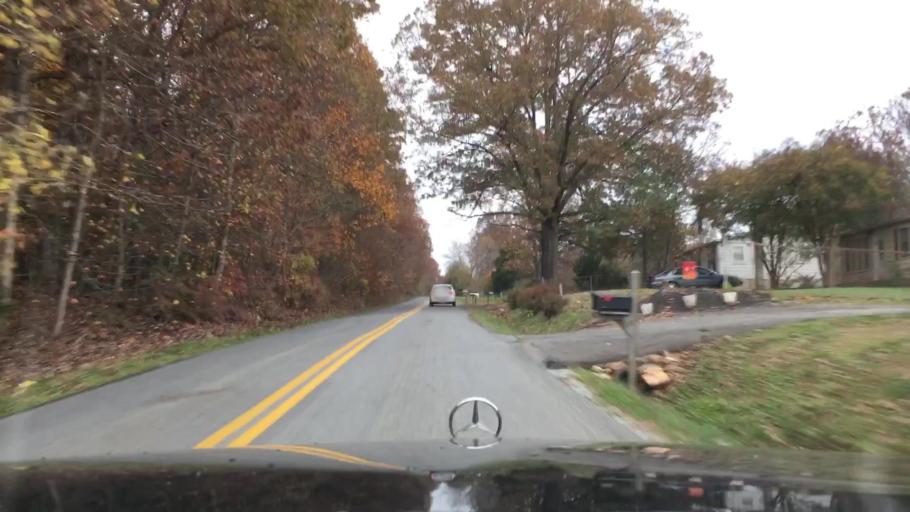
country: US
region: Virginia
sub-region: Campbell County
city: Timberlake
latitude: 37.2922
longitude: -79.2784
